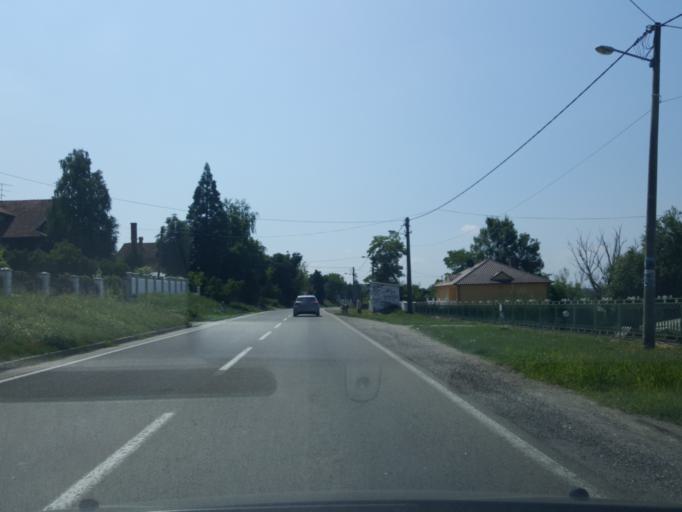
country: RS
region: Central Serbia
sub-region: Belgrade
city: Mladenovac
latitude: 44.4835
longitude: 20.6589
